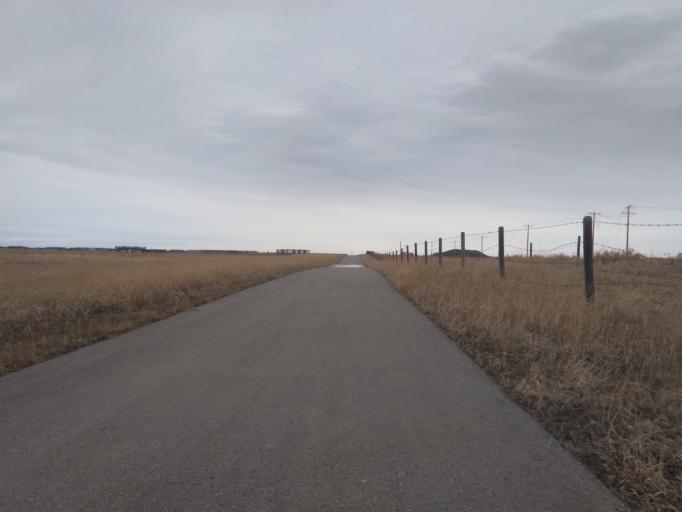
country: CA
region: Alberta
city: Calgary
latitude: 51.1409
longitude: -113.9466
